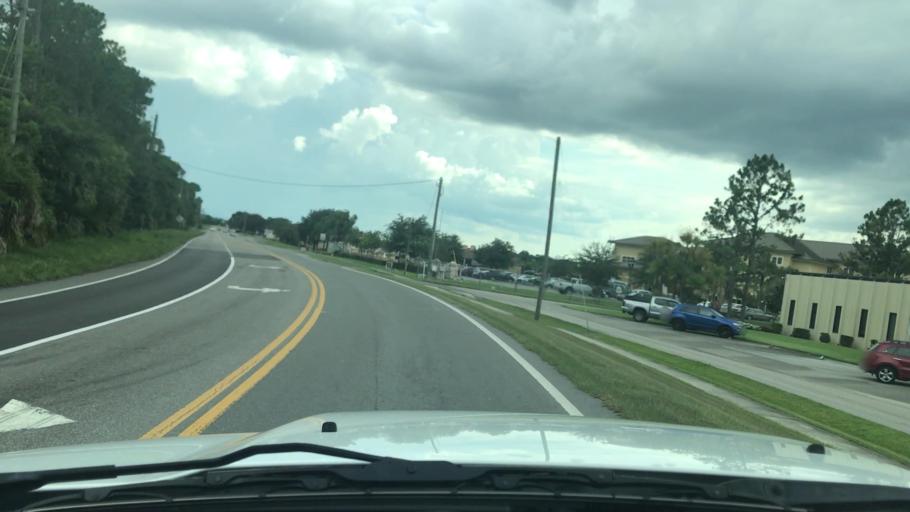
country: US
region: Florida
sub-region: Polk County
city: Cypress Gardens
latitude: 28.0146
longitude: -81.6778
